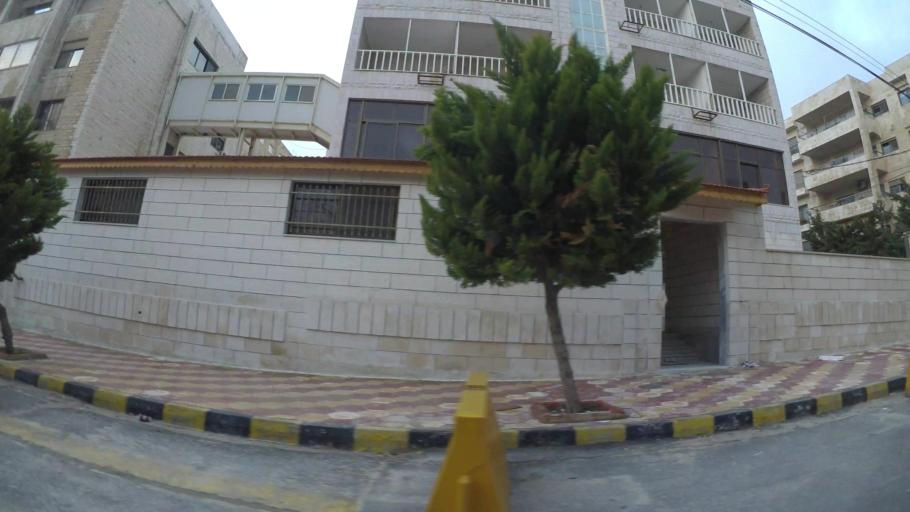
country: JO
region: Amman
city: Amman
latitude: 31.9620
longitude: 35.8866
